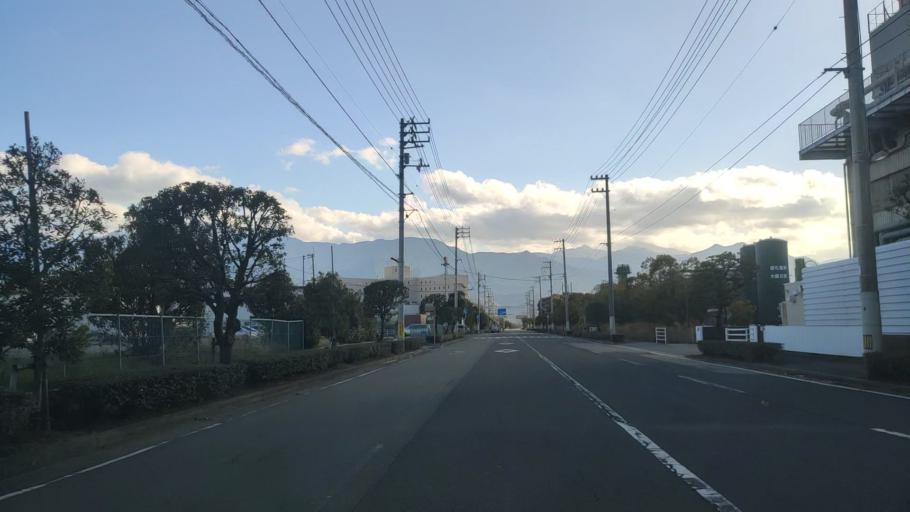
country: JP
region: Ehime
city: Saijo
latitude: 33.9380
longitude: 133.1919
